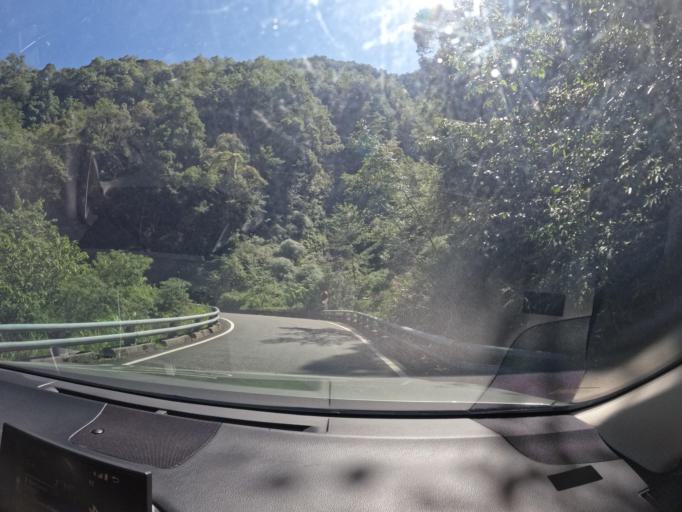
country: TW
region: Taiwan
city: Yujing
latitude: 23.2797
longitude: 120.8751
